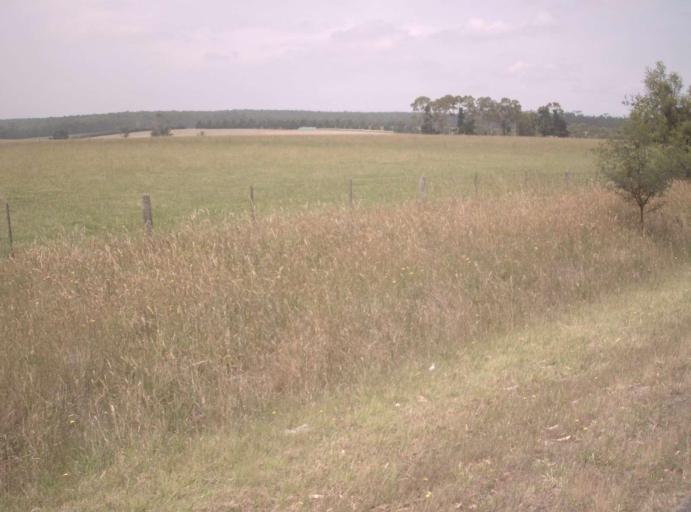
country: AU
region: Victoria
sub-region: Latrobe
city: Traralgon
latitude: -38.4942
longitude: 146.7126
